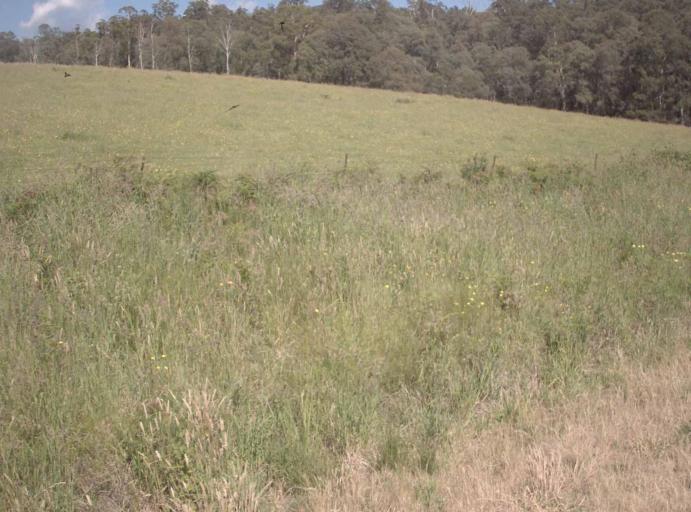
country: AU
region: New South Wales
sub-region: Bombala
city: Bombala
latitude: -37.2000
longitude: 148.7273
